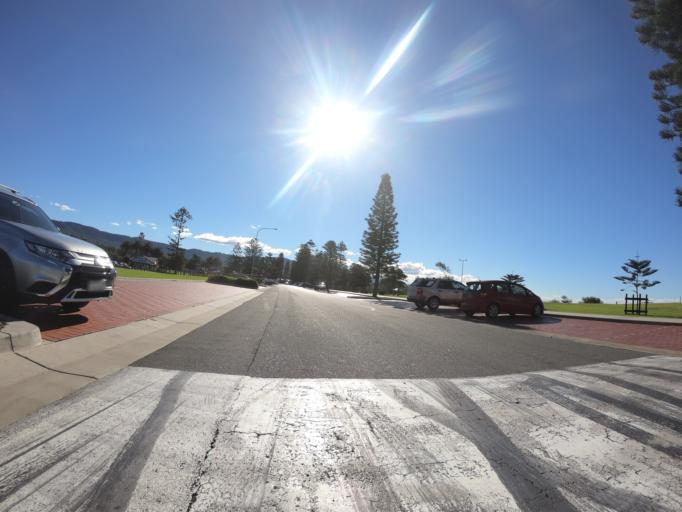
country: AU
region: New South Wales
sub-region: Wollongong
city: Wollongong
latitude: -34.4115
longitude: 150.9014
